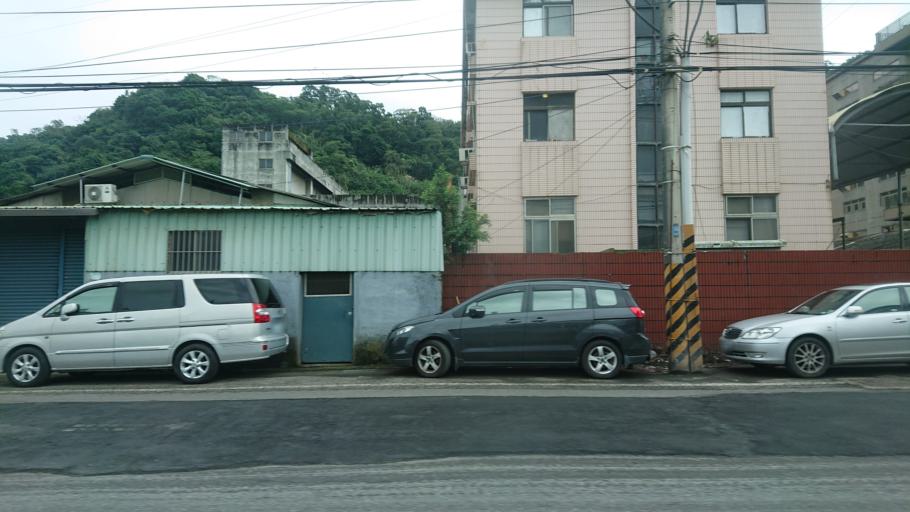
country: TW
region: Taiwan
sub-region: Taoyuan
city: Taoyuan
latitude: 24.9422
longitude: 121.3995
